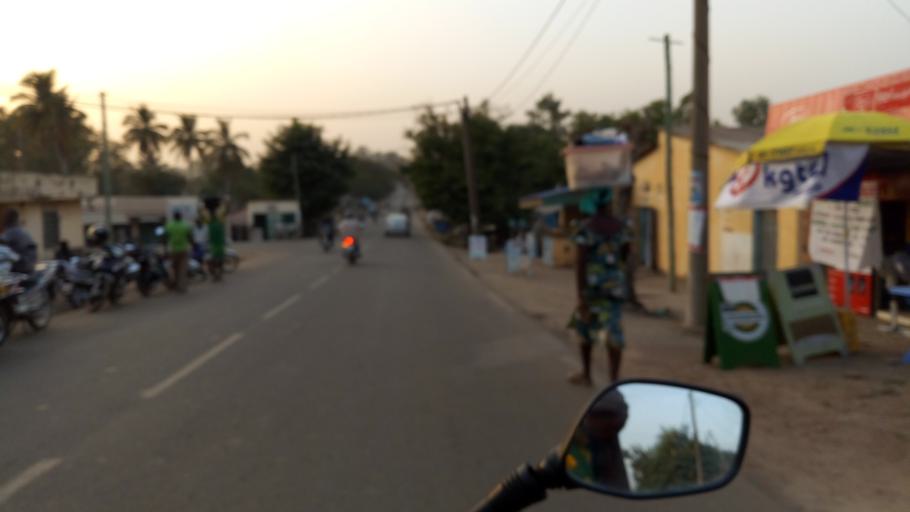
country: TG
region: Kara
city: Kara
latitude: 9.5484
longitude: 1.1885
